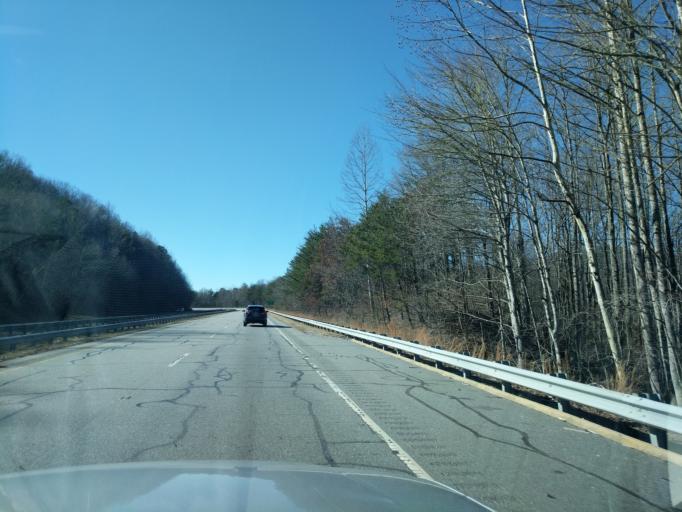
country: US
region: North Carolina
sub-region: Swain County
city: Bryson City
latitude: 35.4049
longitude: -83.4649
